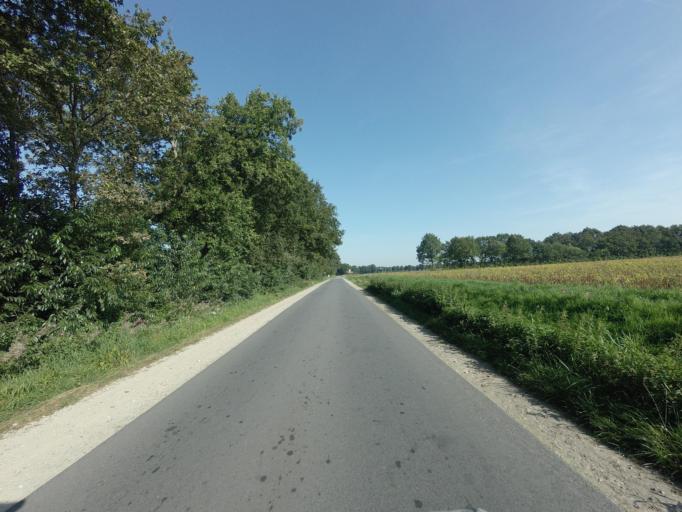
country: DE
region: Lower Saxony
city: Laar
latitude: 52.5902
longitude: 6.7794
